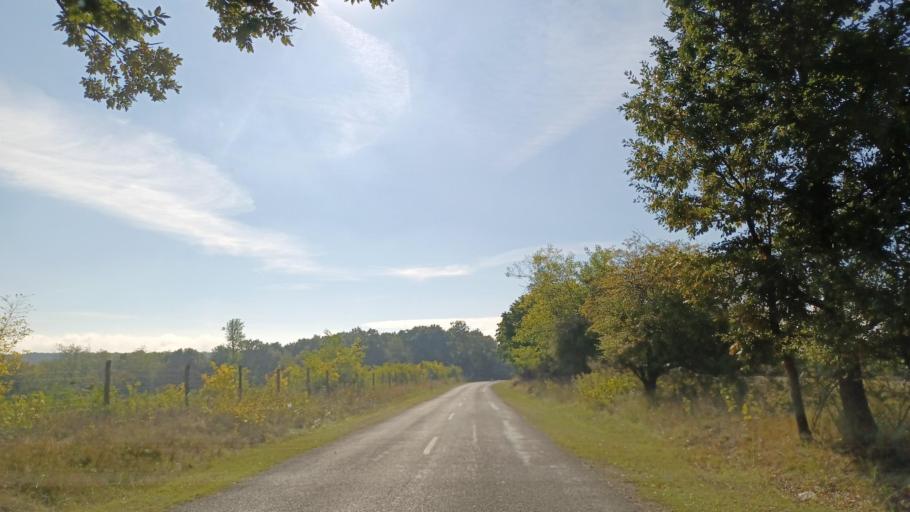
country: HU
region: Tolna
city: Pincehely
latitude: 46.6713
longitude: 18.4768
